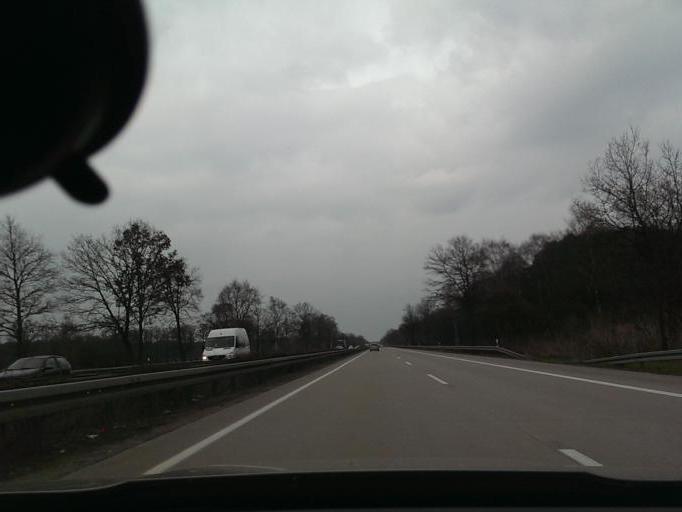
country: DE
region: Lower Saxony
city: Elze
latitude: 52.5210
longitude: 9.7794
